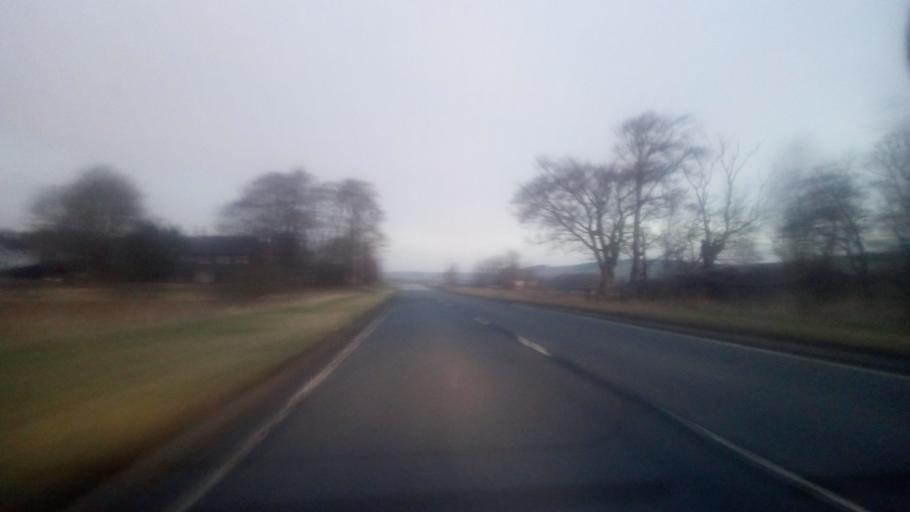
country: GB
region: Scotland
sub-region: The Scottish Borders
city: Lauder
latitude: 55.7477
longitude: -2.7717
